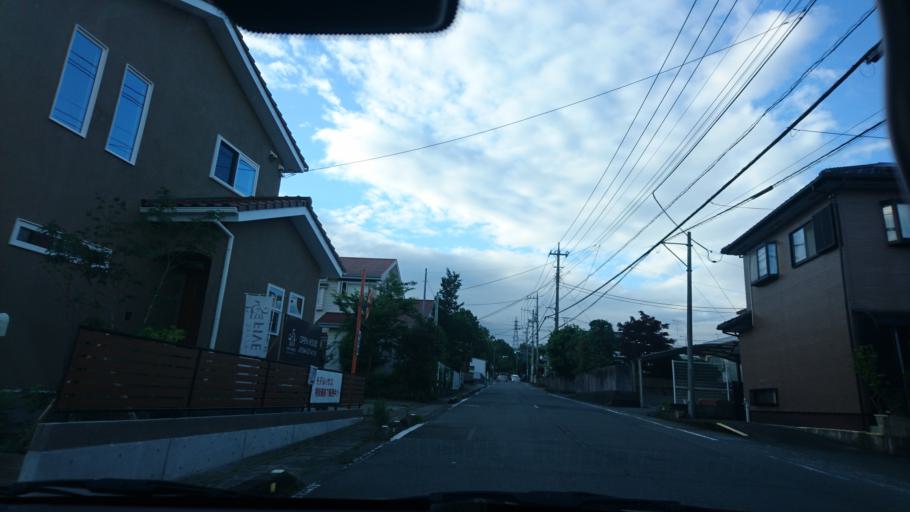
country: JP
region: Shizuoka
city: Fujinomiya
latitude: 35.2359
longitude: 138.6231
